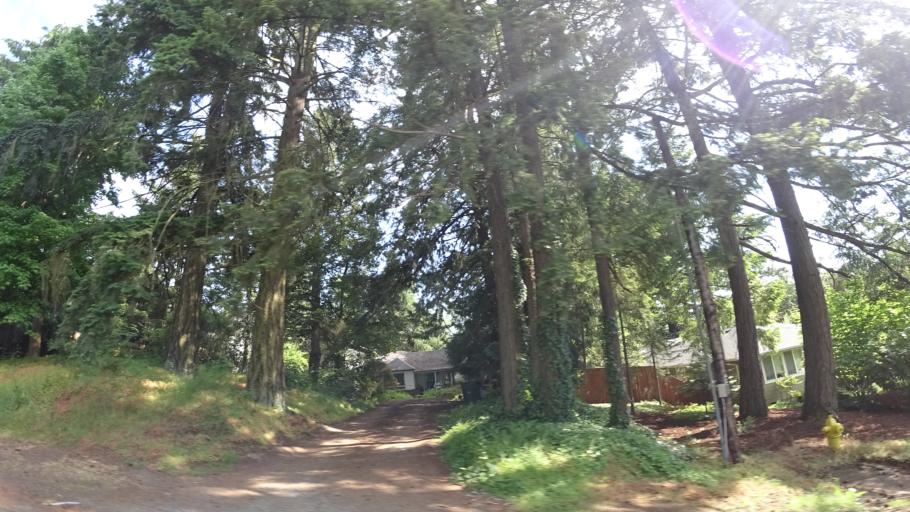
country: US
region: Oregon
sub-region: Washington County
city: Garden Home-Whitford
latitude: 45.4567
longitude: -122.7516
